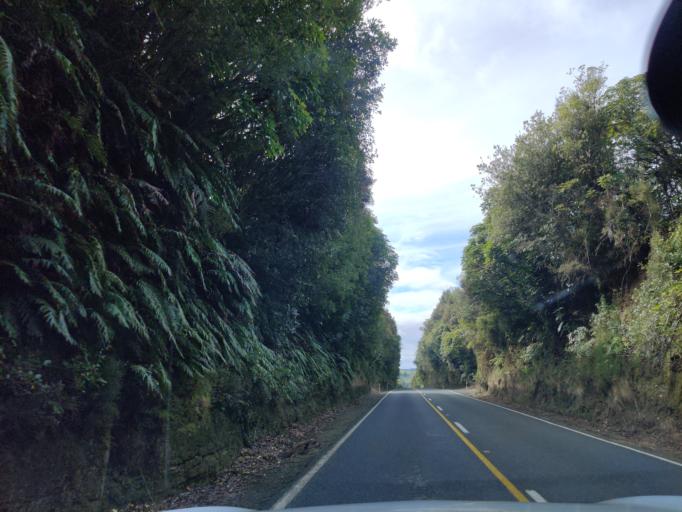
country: NZ
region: Waikato
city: Turangi
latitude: -38.7082
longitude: 175.6735
